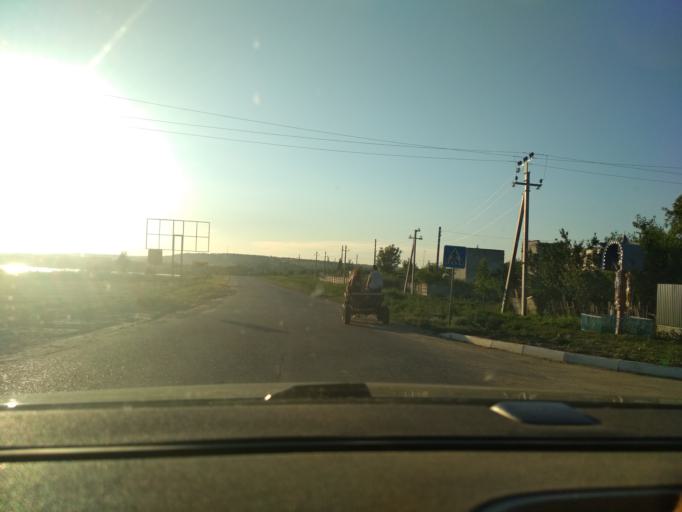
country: RO
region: Iasi
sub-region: Comuna Grozesti
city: Grozesti
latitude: 47.0106
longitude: 28.0736
